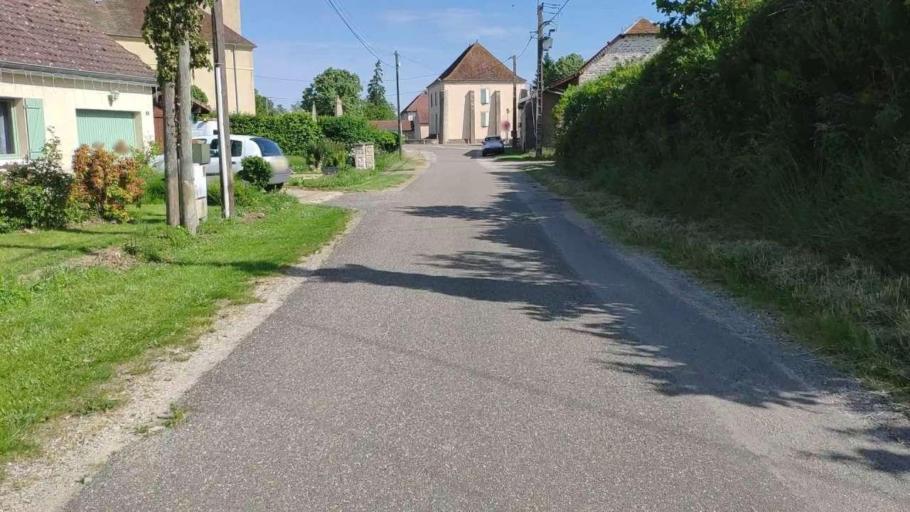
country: FR
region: Franche-Comte
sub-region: Departement du Jura
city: Bletterans
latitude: 46.7110
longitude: 5.4537
